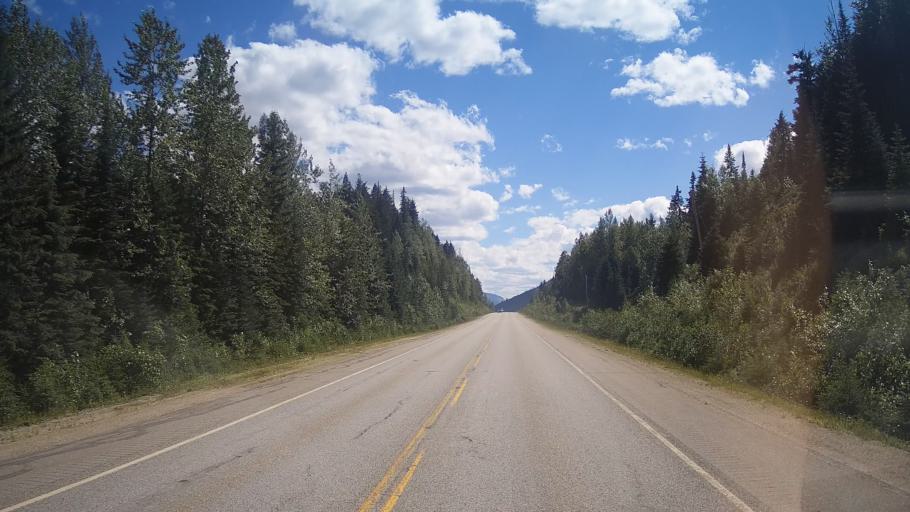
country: CA
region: Alberta
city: Jasper Park Lodge
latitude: 52.5522
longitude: -119.1121
